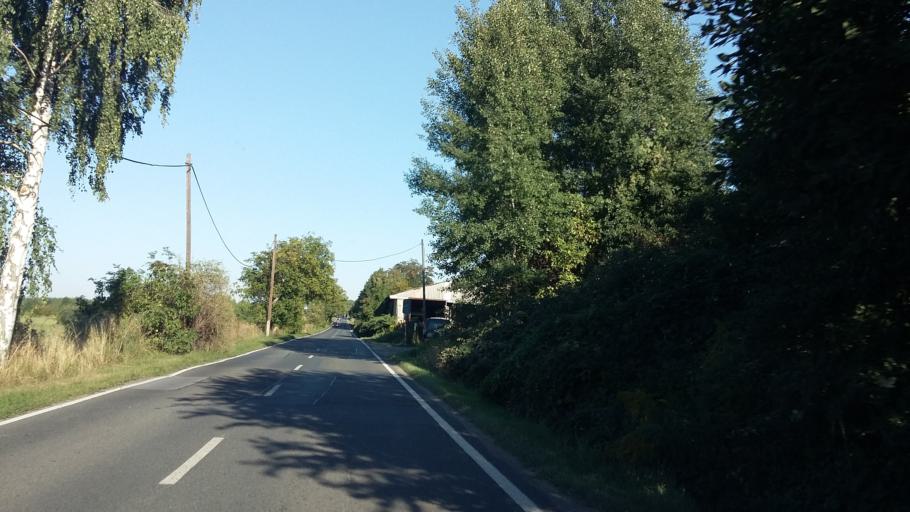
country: CZ
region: Praha
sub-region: Praha 18
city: Letnany
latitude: 50.1360
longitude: 14.5262
